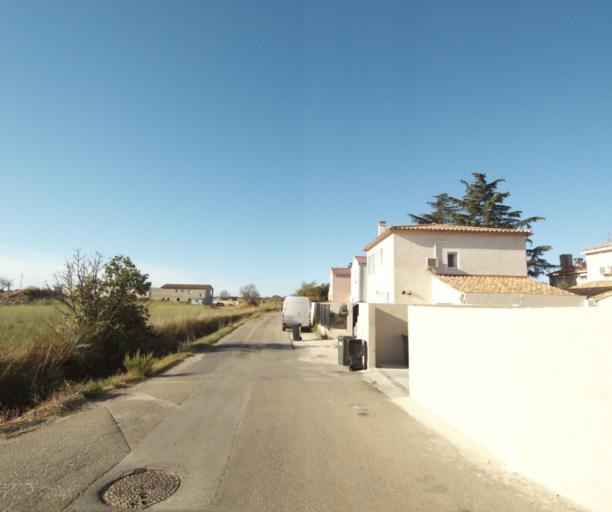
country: FR
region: Languedoc-Roussillon
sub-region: Departement du Gard
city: Bouillargues
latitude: 43.7915
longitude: 4.4362
